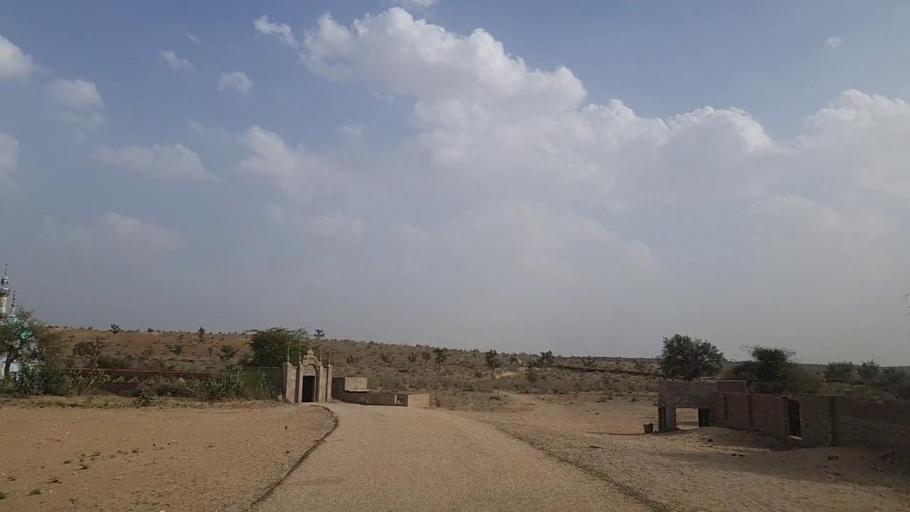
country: PK
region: Sindh
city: Islamkot
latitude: 24.8611
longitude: 70.1129
